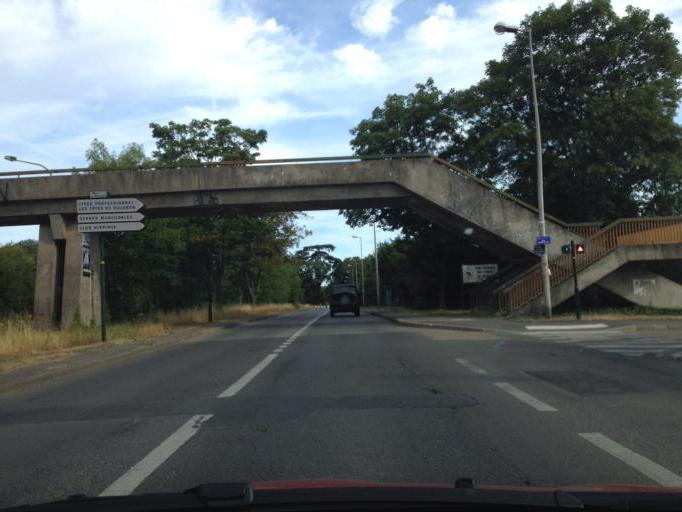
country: FR
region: Ile-de-France
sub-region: Departement des Hauts-de-Seine
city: Meudon
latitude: 48.7936
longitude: 2.2192
